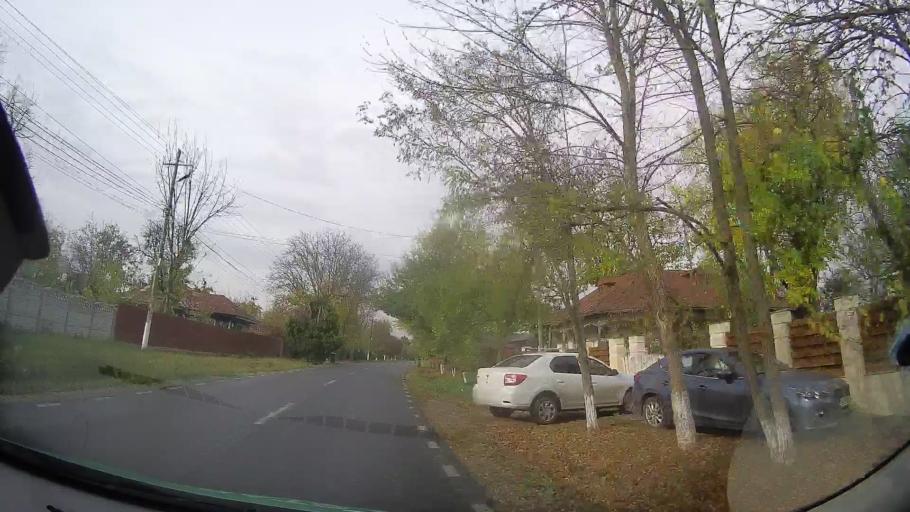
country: RO
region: Ialomita
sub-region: Comuna Fierbinti-Targ
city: Fierbinti-Targ
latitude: 44.7010
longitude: 26.3281
